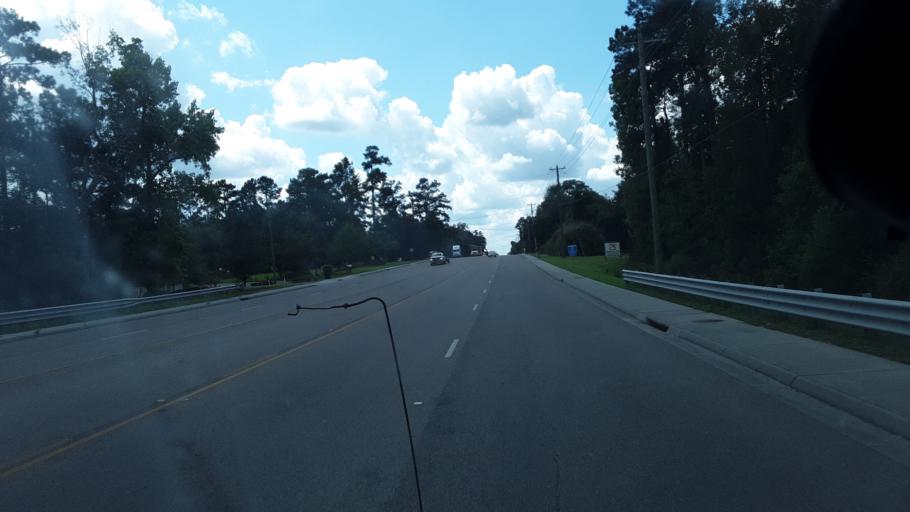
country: US
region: South Carolina
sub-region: Berkeley County
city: Moncks Corner
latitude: 33.1206
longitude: -80.0693
